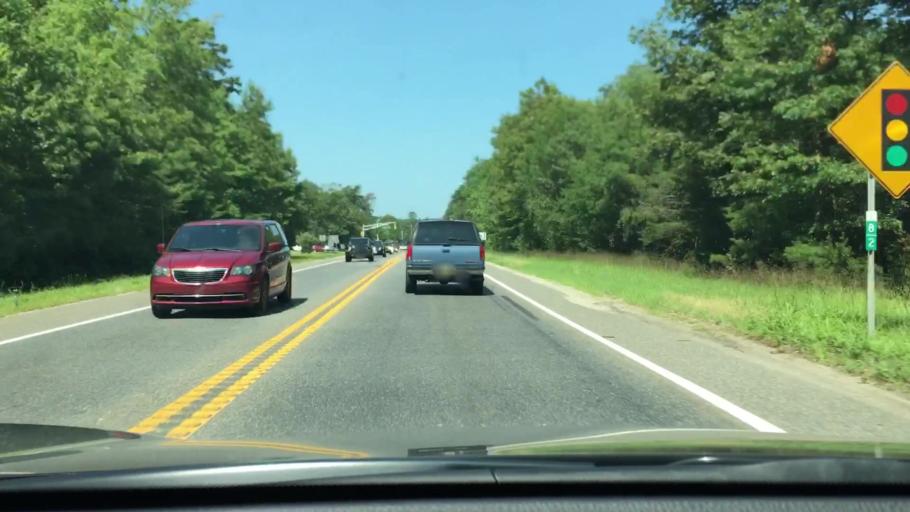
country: US
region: New Jersey
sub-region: Cumberland County
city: Laurel Lake
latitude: 39.2899
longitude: -74.9647
